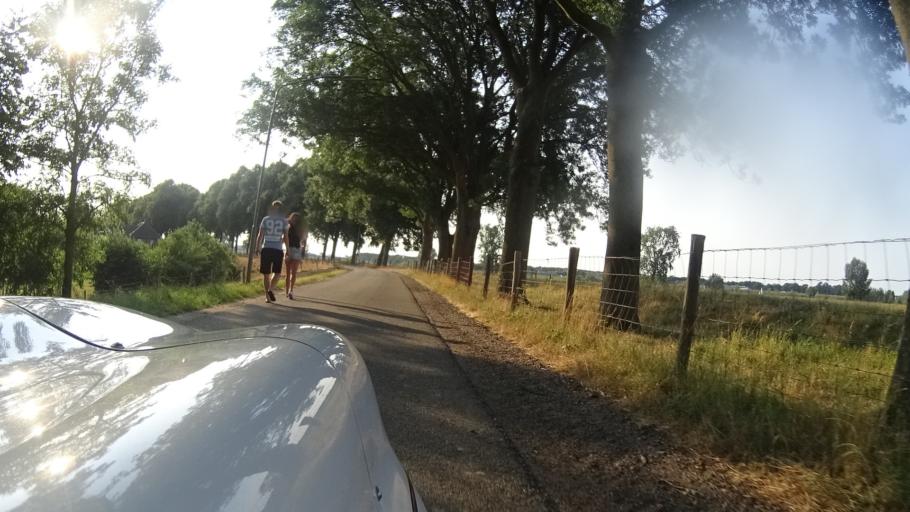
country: NL
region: North Brabant
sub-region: Gemeente Landerd
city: Reek
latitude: 51.7892
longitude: 5.6799
